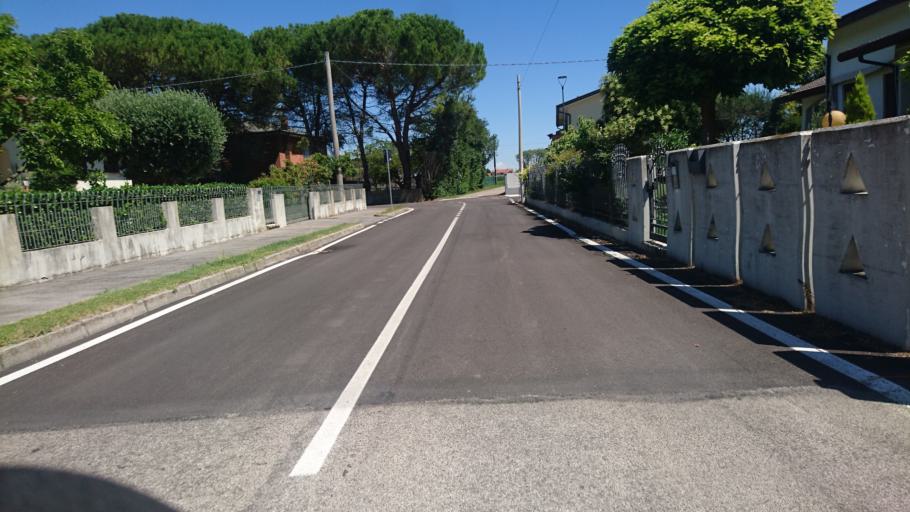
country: IT
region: Veneto
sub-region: Provincia di Padova
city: Campagnola
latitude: 45.2798
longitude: 12.0016
